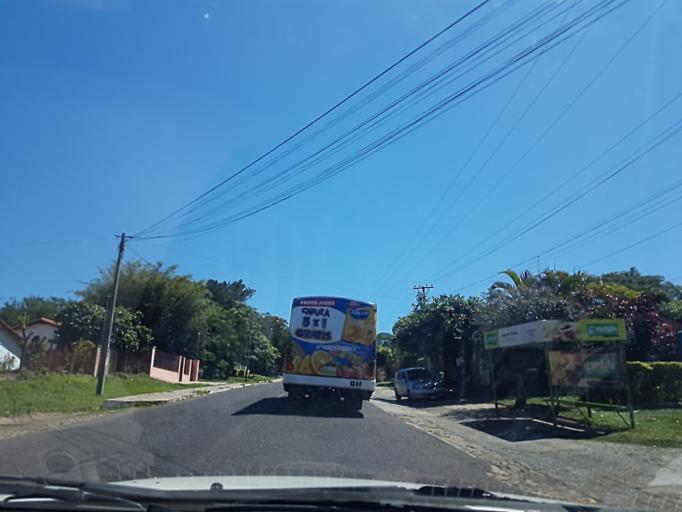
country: PY
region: Cordillera
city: Altos
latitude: -25.2598
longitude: -57.2482
